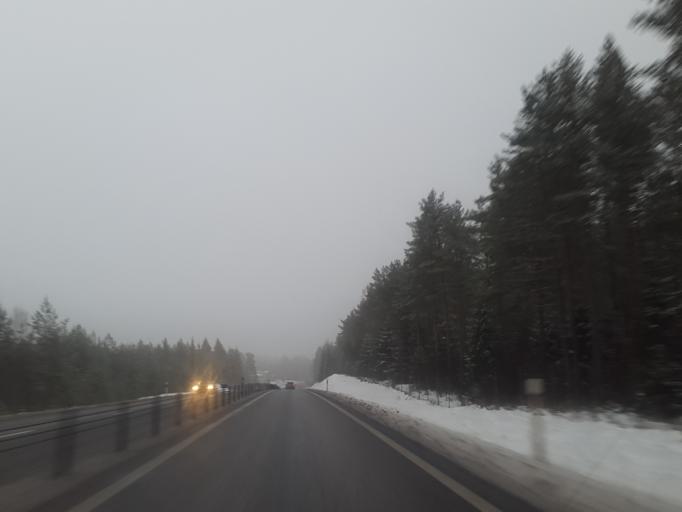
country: SE
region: Joenkoeping
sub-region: Mullsjo Kommun
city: Mullsjoe
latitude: 57.7669
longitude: 13.8163
